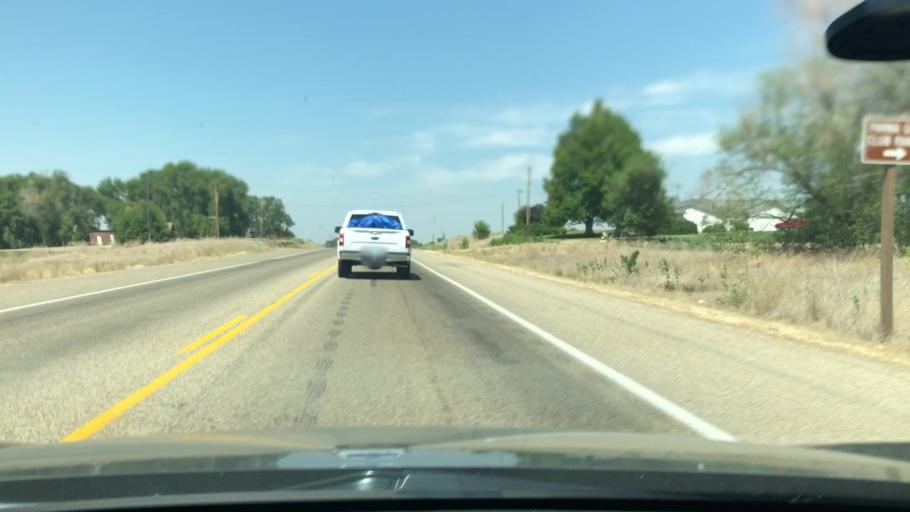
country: US
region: Idaho
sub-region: Canyon County
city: Parma
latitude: 43.8351
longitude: -116.9545
